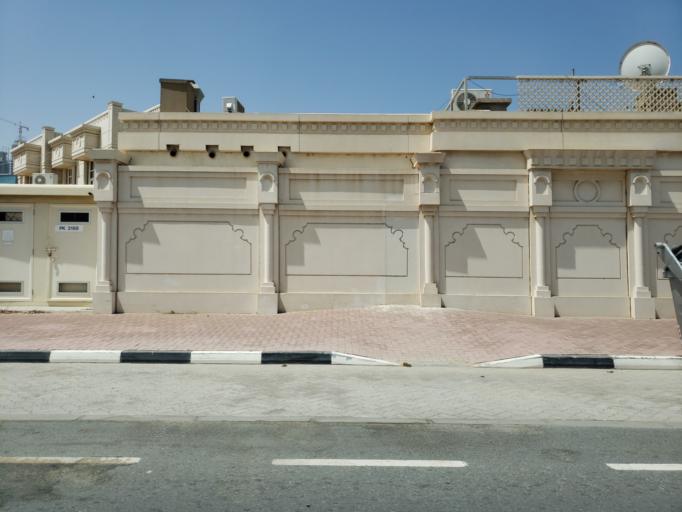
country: AE
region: Dubai
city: Dubai
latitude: 25.1178
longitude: 55.1818
